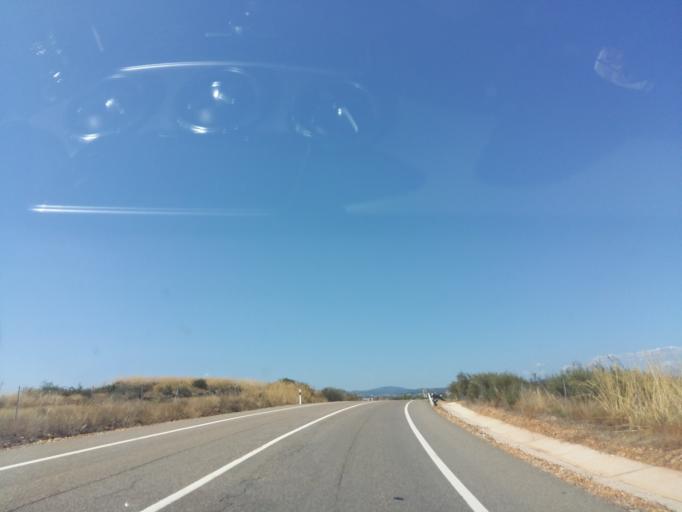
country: ES
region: Castille and Leon
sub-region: Provincia de Leon
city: San Justo de la Vega
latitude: 42.4362
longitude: -6.0369
